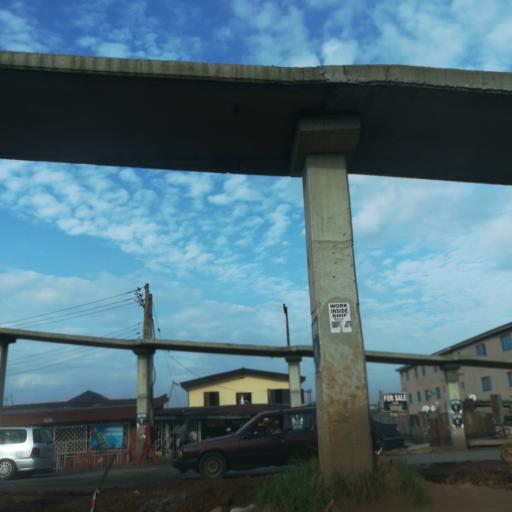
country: NG
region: Lagos
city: Oshodi
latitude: 6.5758
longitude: 3.3437
